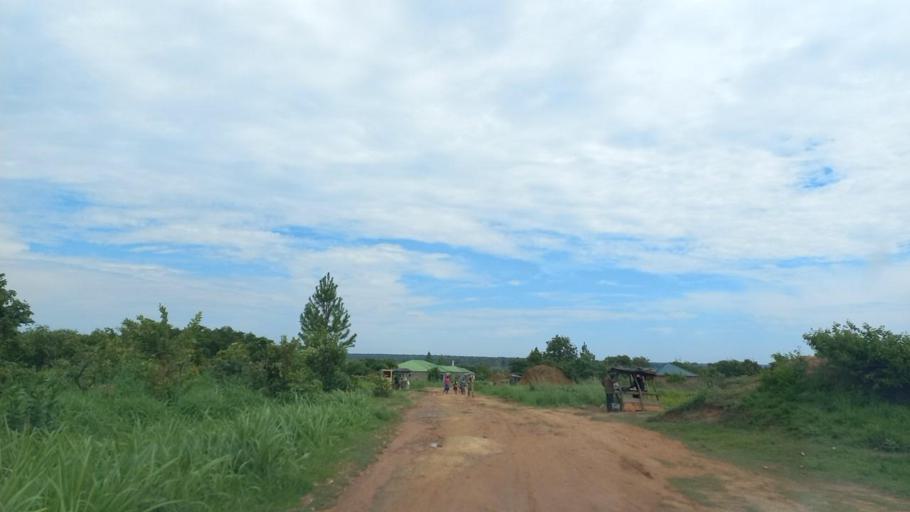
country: ZM
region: Copperbelt
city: Kitwe
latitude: -12.8708
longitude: 28.3341
